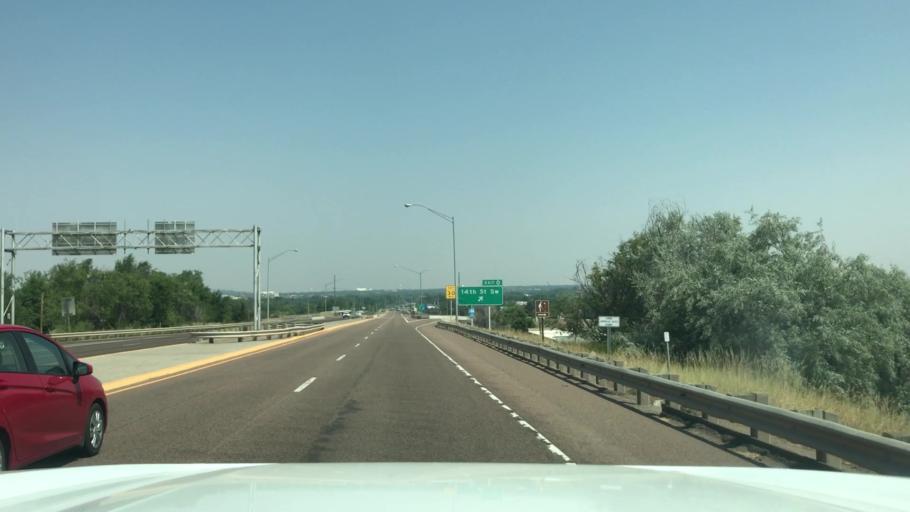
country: US
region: Montana
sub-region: Cascade County
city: Great Falls
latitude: 47.4858
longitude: -111.3413
